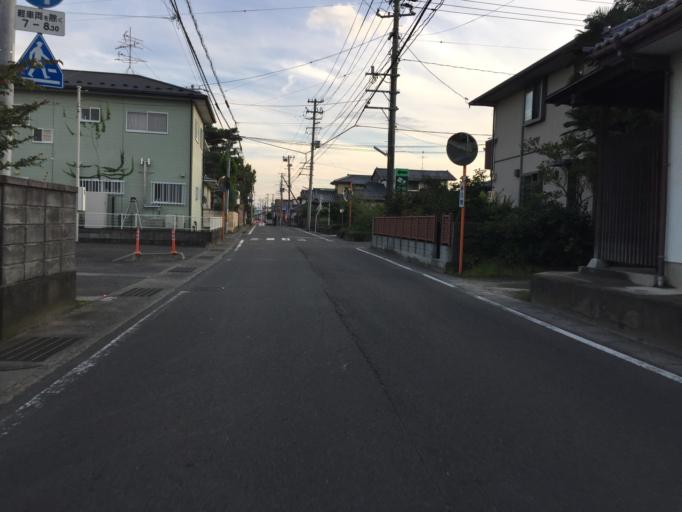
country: JP
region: Fukushima
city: Hobaramachi
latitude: 37.8228
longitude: 140.5027
